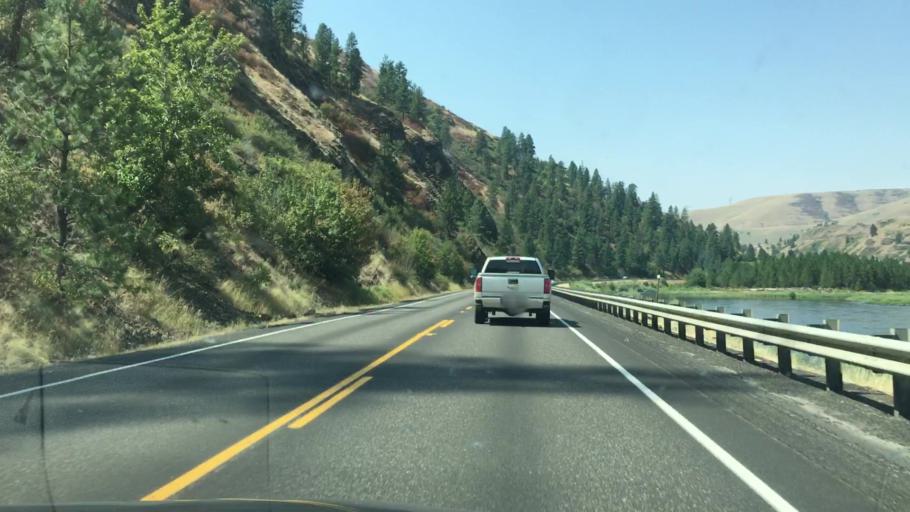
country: US
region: Idaho
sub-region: Nez Perce County
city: Lapwai
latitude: 46.4895
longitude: -116.7316
